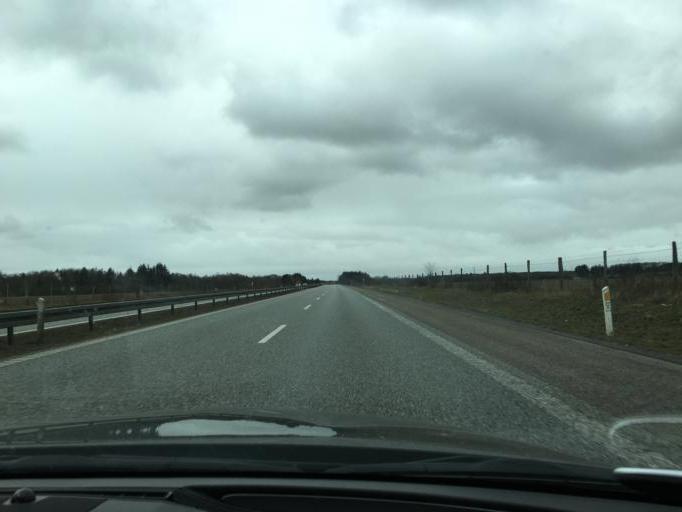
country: DK
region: South Denmark
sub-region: Esbjerg Kommune
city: Bramming
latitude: 55.5110
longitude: 8.7418
